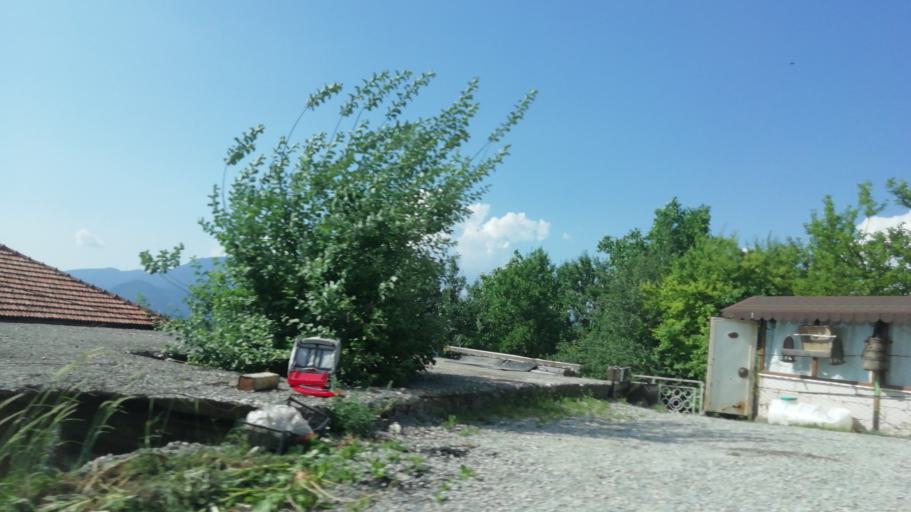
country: TR
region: Karabuk
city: Karabuk
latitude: 41.1257
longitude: 32.5781
